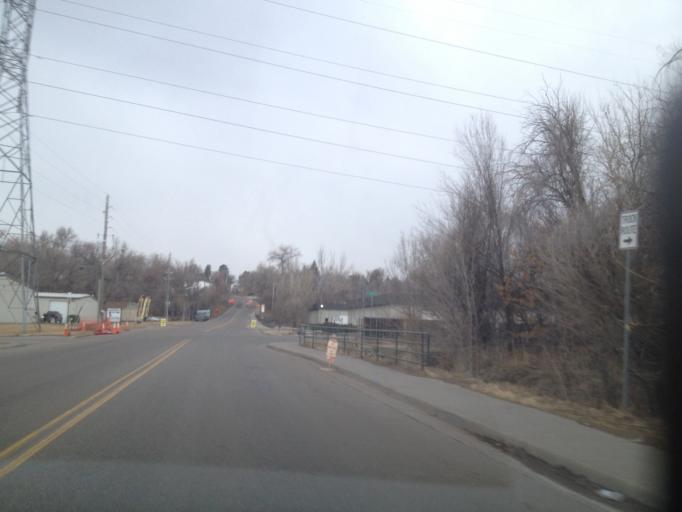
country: US
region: Colorado
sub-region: Adams County
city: Berkley
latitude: 39.7953
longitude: -105.0439
